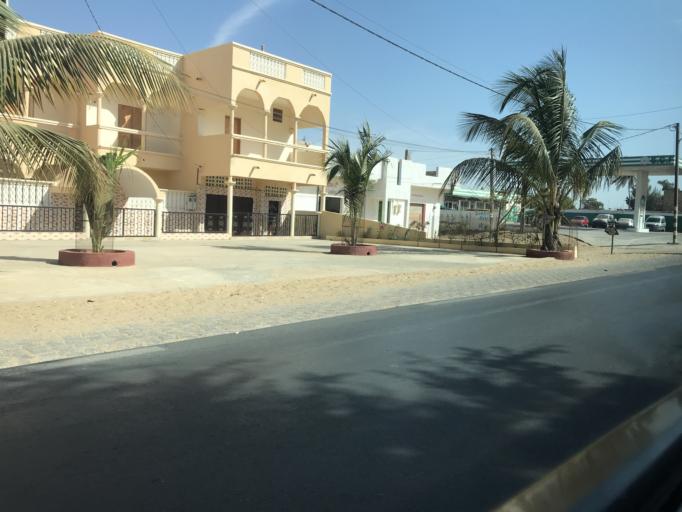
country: SN
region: Saint-Louis
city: Saint-Louis
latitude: 16.0344
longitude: -16.4696
